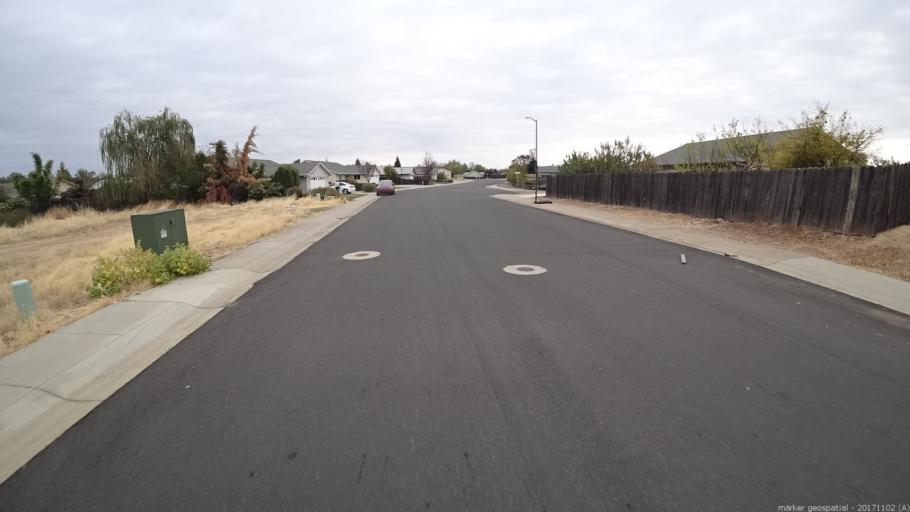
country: US
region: California
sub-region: Shasta County
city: Redding
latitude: 40.6184
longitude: -122.4356
